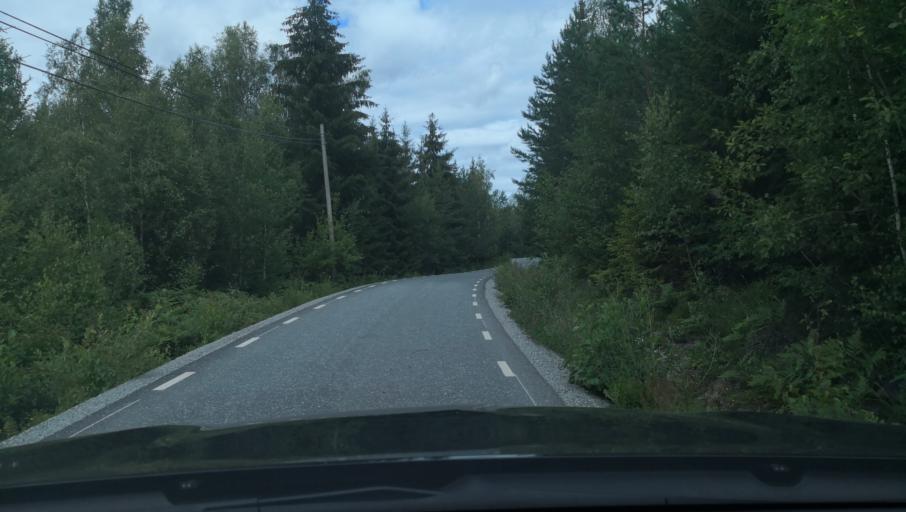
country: SE
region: Vaestmanland
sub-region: Hallstahammars Kommun
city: Hallstahammar
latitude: 59.6218
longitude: 16.1405
